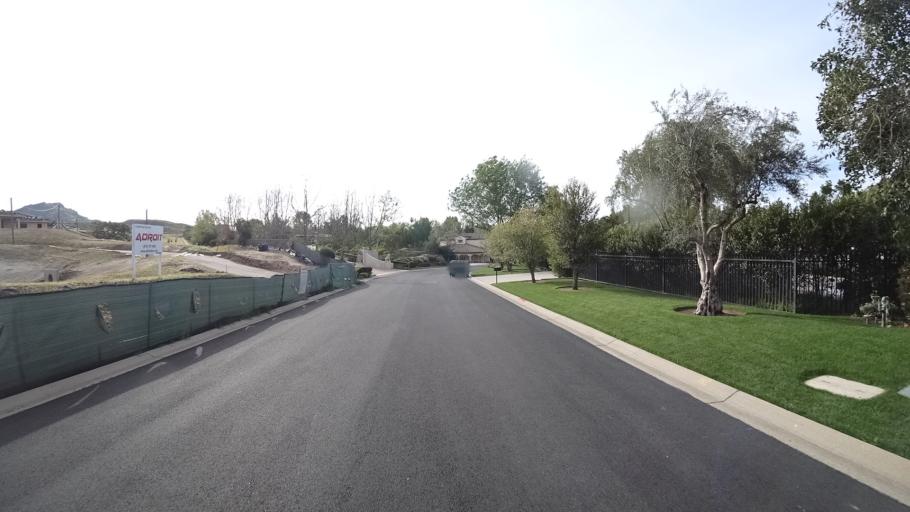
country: US
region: California
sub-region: Ventura County
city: Thousand Oaks
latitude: 34.2003
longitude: -118.8208
